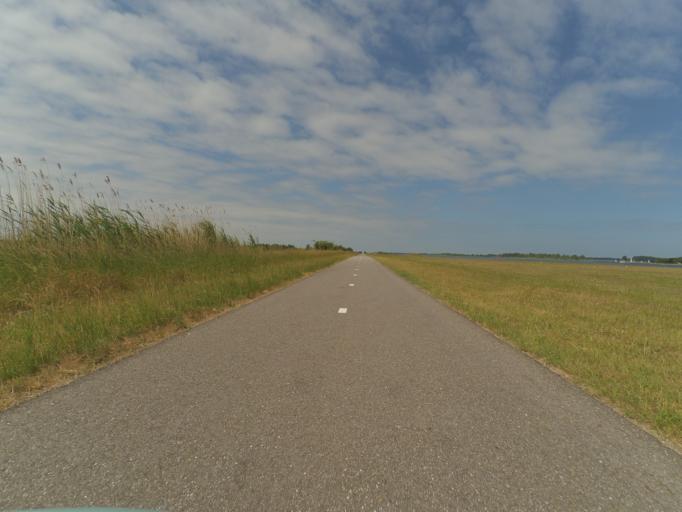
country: NL
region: Zeeland
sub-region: Gemeente Noord-Beveland
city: Kamperland
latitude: 51.5408
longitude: 3.7900
